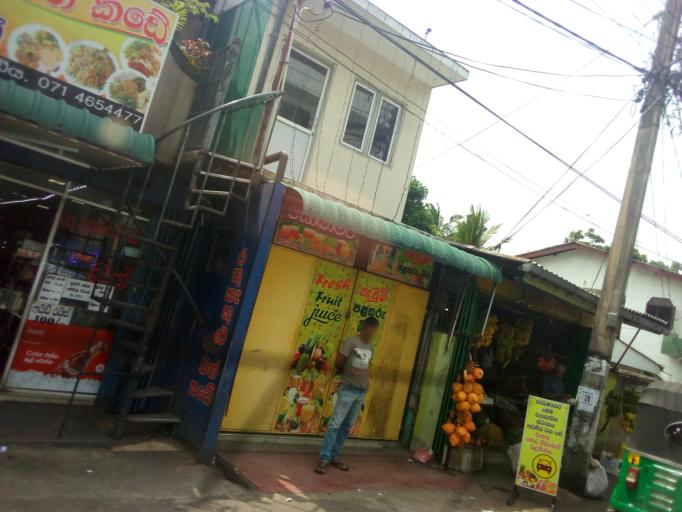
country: LK
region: Western
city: Galkissa
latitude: 6.8379
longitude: 79.8848
